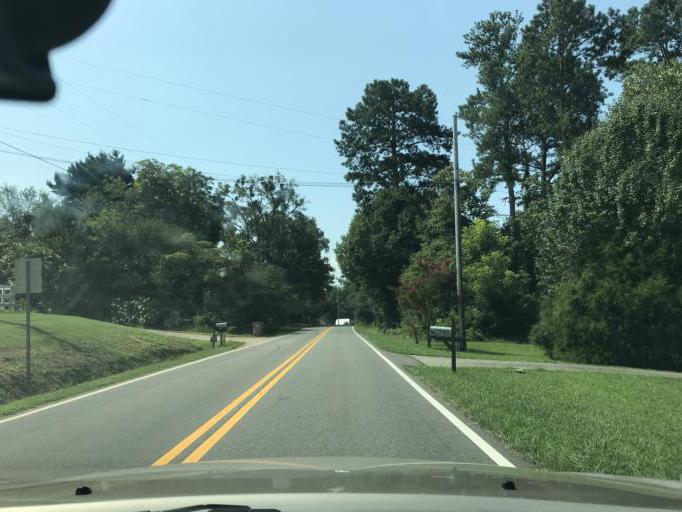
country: US
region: Georgia
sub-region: Hall County
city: Flowery Branch
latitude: 34.2433
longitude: -83.9972
